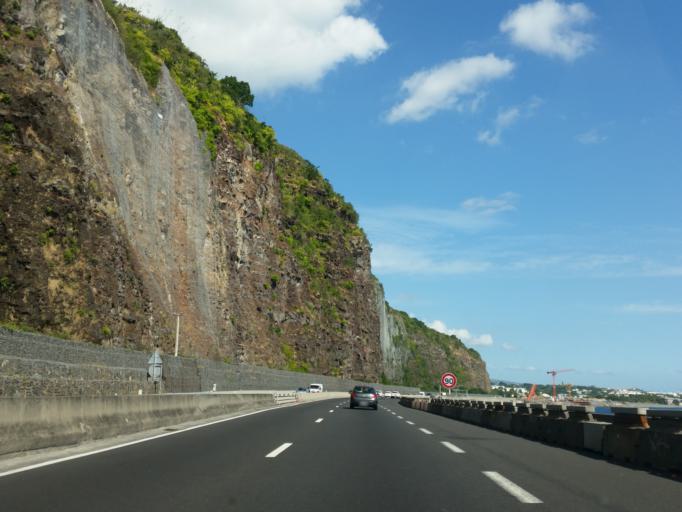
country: RE
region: Reunion
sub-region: Reunion
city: La Possession
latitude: -20.9127
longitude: 55.3515
